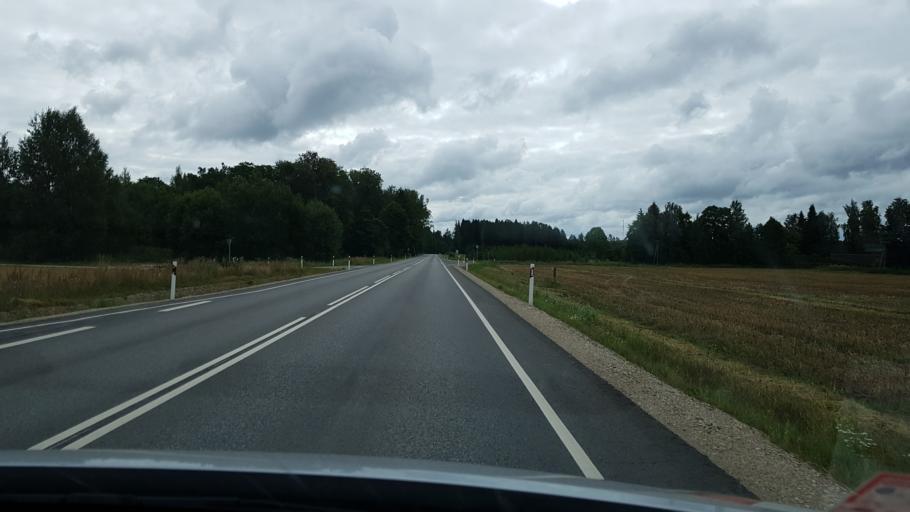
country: EE
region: Polvamaa
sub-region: Polva linn
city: Polva
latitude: 58.0270
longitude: 27.1561
